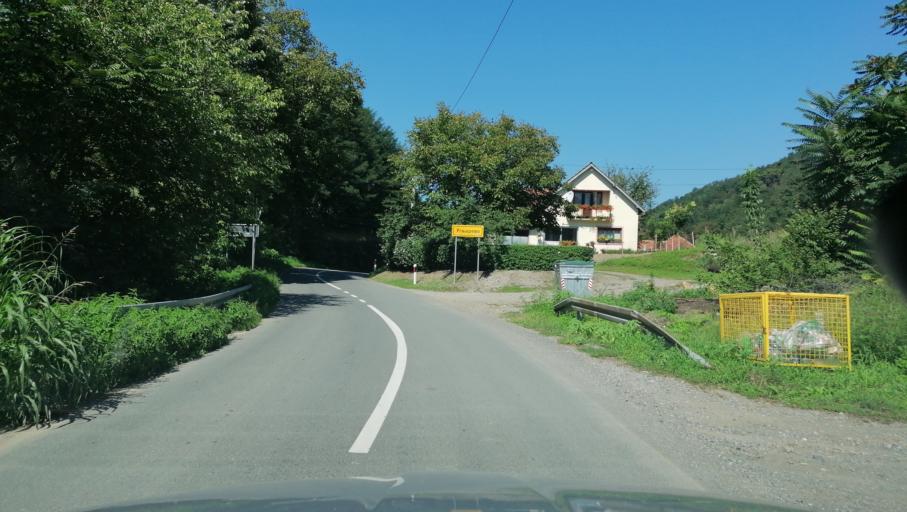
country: RS
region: Central Serbia
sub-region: Raski Okrug
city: Vrnjacka Banja
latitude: 43.6626
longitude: 20.9237
